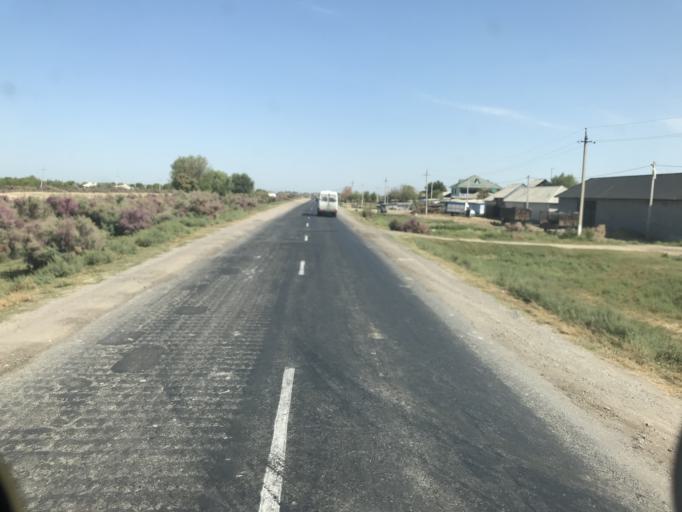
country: KZ
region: Ongtustik Qazaqstan
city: Myrzakent
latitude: 40.7307
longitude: 68.5365
